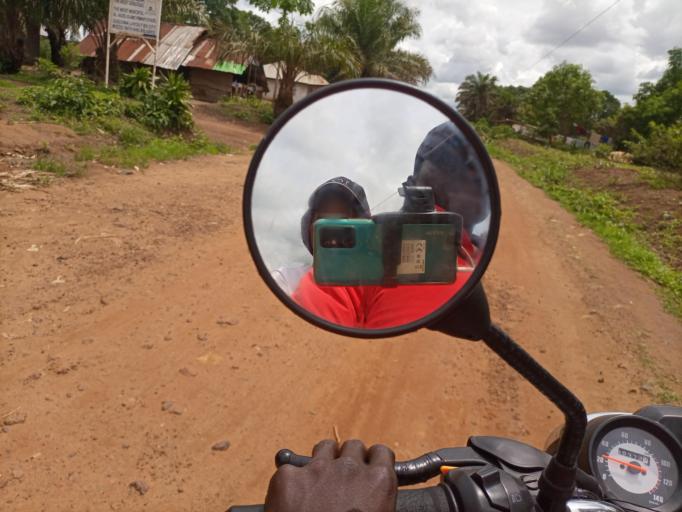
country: SL
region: Southern Province
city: Bo
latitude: 7.9676
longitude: -11.7160
